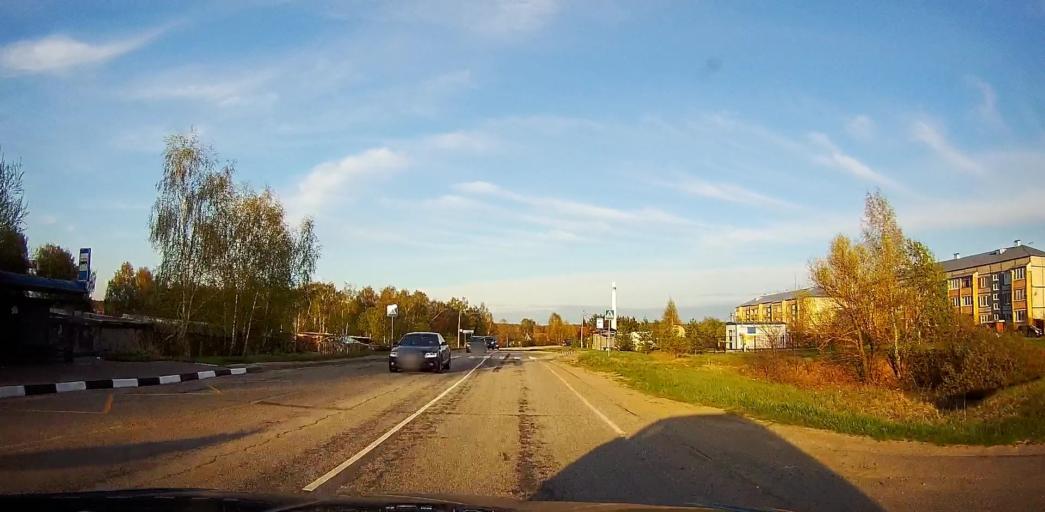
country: RU
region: Moskovskaya
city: Meshcherino
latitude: 55.2339
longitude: 38.3598
